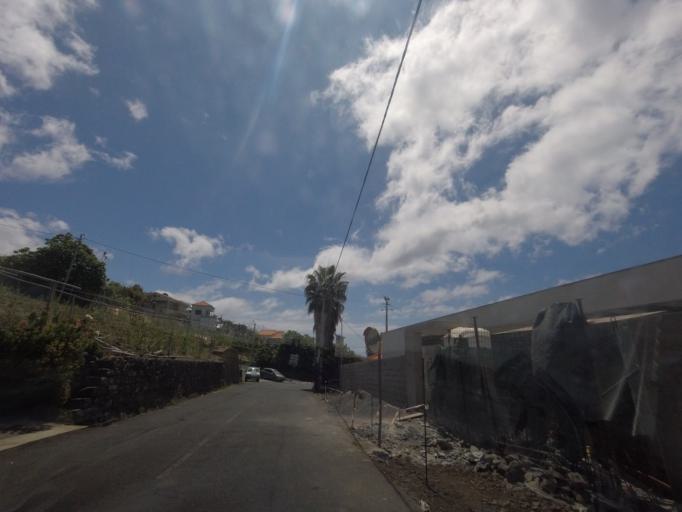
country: PT
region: Madeira
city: Ponta do Sol
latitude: 32.6824
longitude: -17.0835
